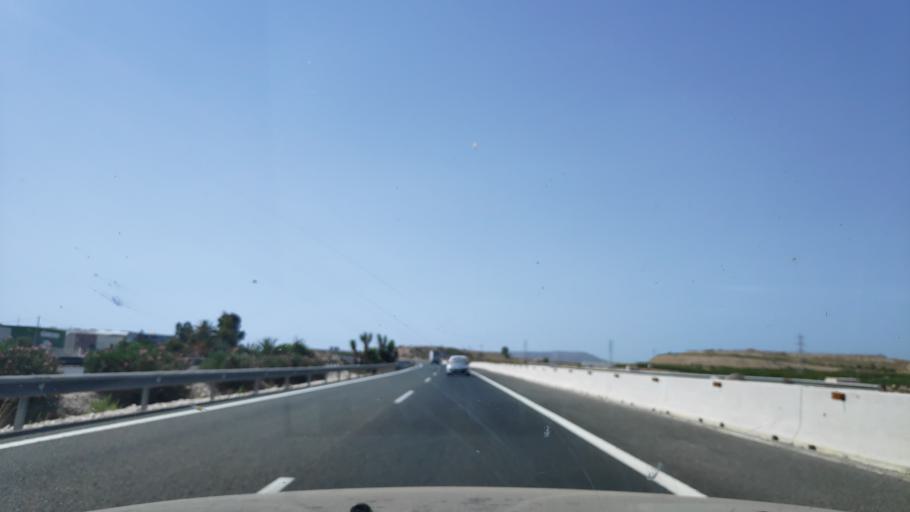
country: ES
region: Murcia
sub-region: Murcia
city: Blanca
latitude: 38.1922
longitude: -1.3308
